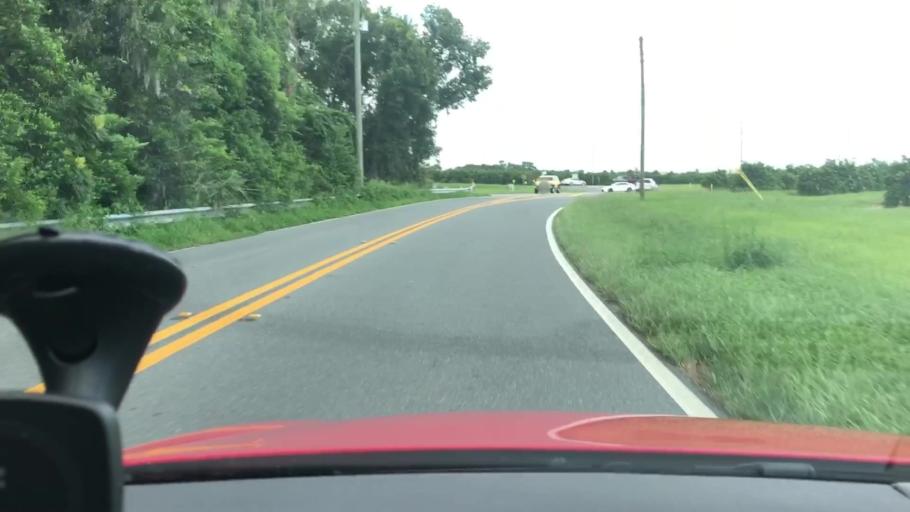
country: US
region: Florida
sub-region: Lake County
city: Mount Dora
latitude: 28.8318
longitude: -81.6444
